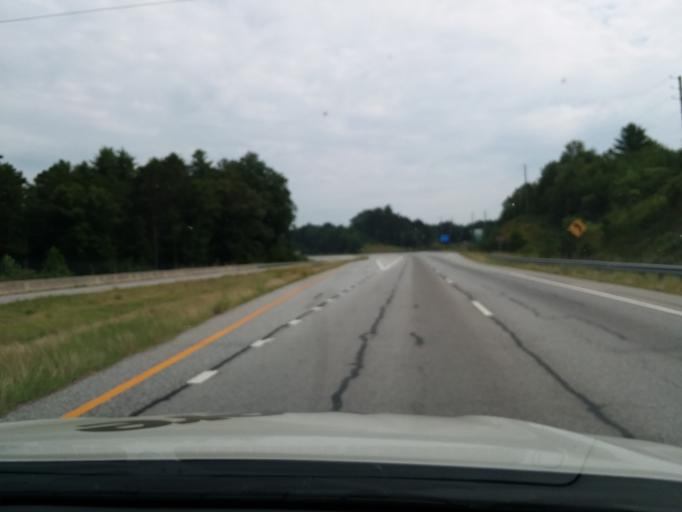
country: US
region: Georgia
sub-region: Rabun County
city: Clayton
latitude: 34.8181
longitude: -83.4238
